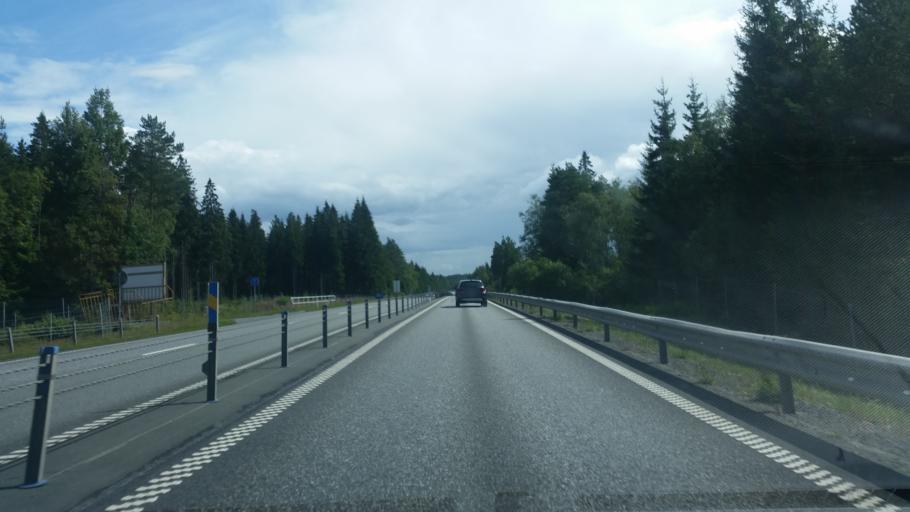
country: SE
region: Joenkoeping
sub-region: Mullsjo Kommun
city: Mullsjoe
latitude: 57.7658
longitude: 13.7571
